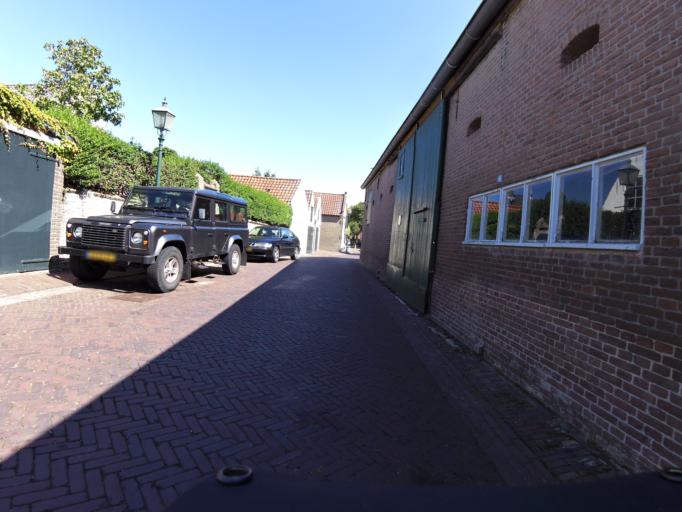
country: NL
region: South Holland
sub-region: Gemeente Goeree-Overflakkee
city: Goedereede
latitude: 51.8174
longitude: 3.9779
